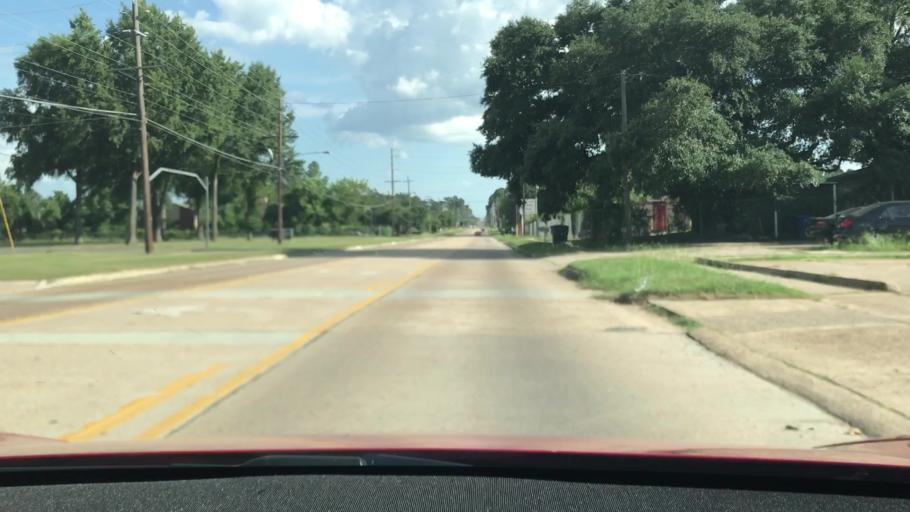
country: US
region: Louisiana
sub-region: Bossier Parish
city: Bossier City
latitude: 32.4070
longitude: -93.7804
